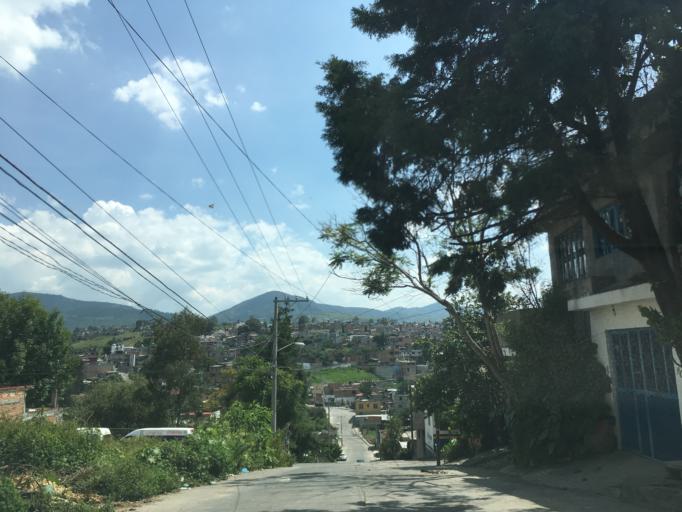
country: MX
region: Michoacan
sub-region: Morelia
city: Montana Monarca (Punta Altozano)
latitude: 19.6707
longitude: -101.1838
